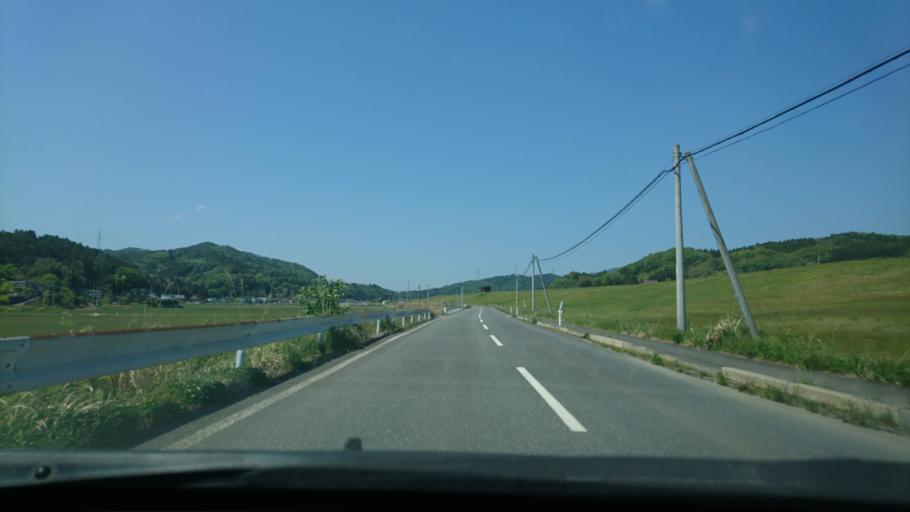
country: JP
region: Iwate
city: Ichinoseki
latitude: 38.9072
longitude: 141.2560
